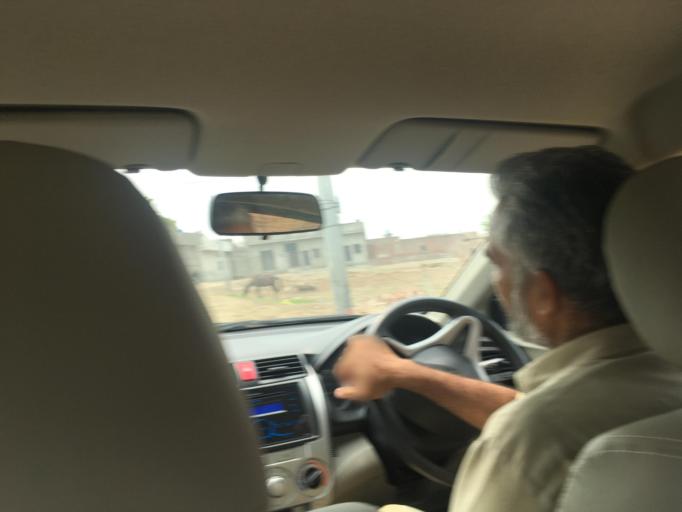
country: PK
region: Punjab
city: Lahore
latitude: 31.6200
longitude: 74.3488
